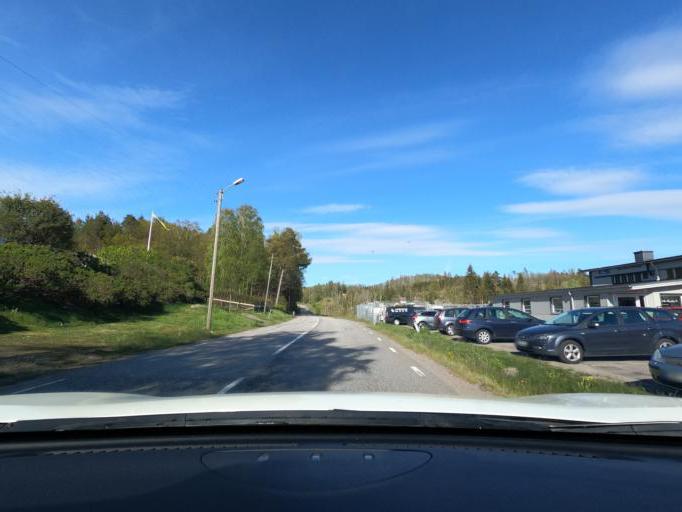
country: SE
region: Vaestra Goetaland
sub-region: Harryda Kommun
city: Landvetter
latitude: 57.6123
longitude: 12.2854
